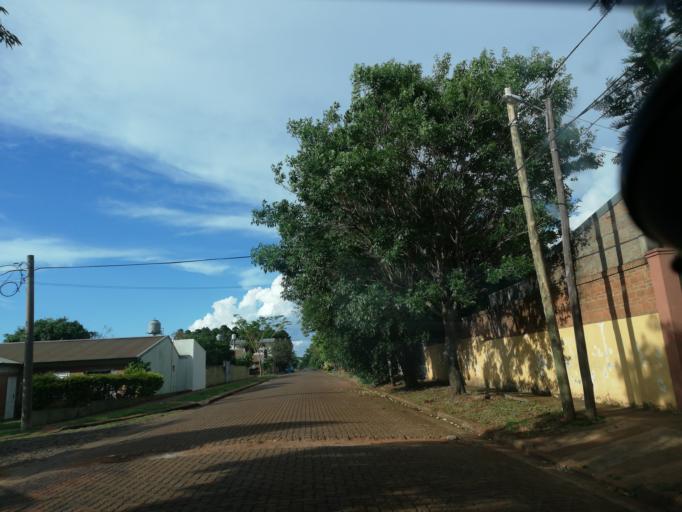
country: AR
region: Misiones
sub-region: Departamento de Capital
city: Posadas
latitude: -27.4195
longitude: -55.9533
